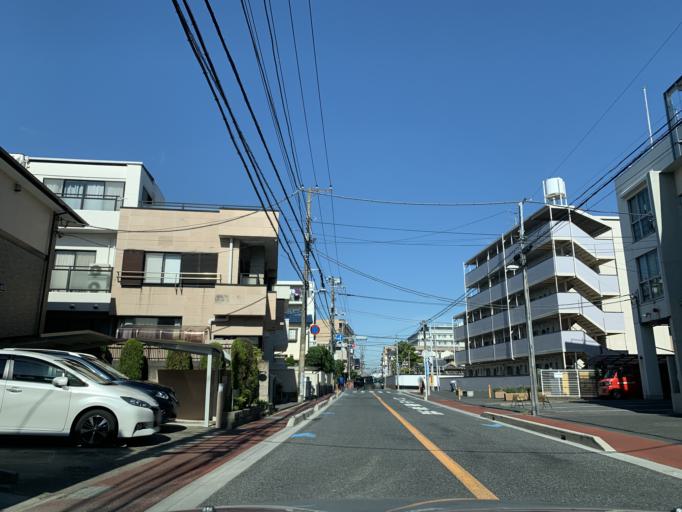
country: JP
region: Tokyo
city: Urayasu
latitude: 35.6688
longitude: 139.8918
